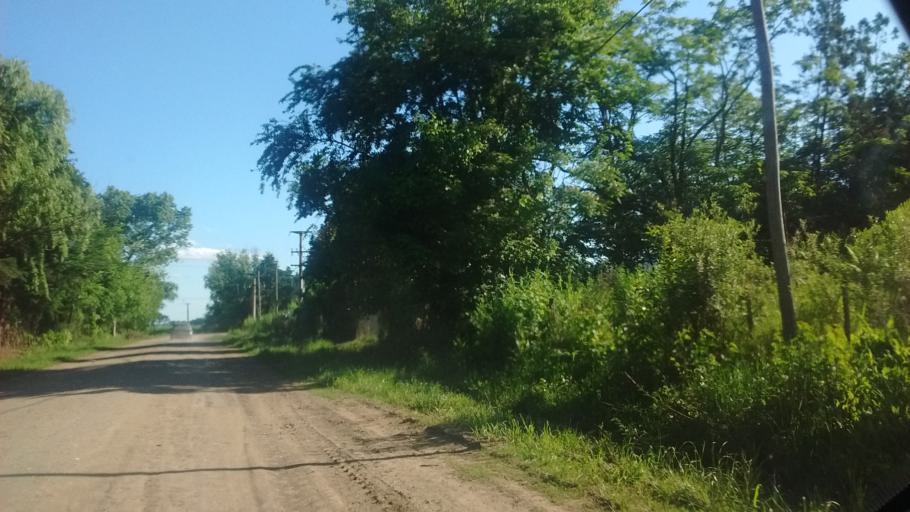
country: AR
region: Santa Fe
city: Funes
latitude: -32.8596
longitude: -60.7942
